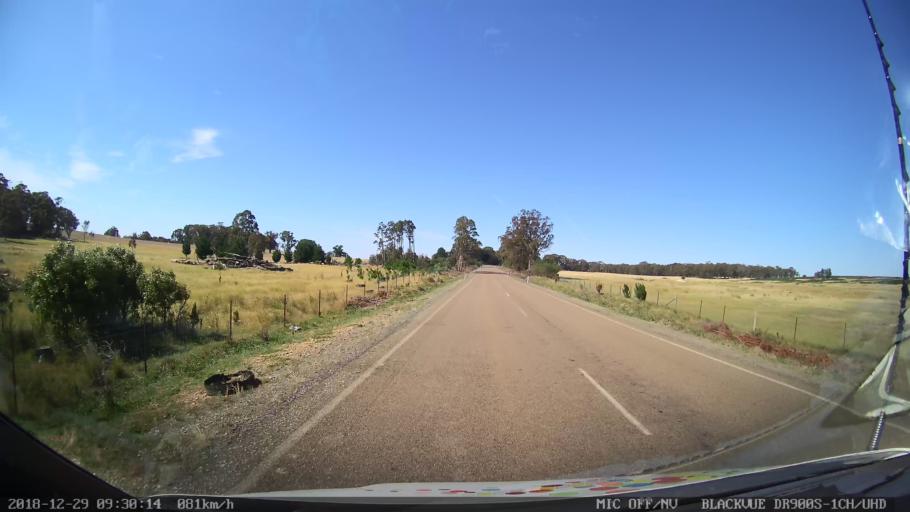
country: AU
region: New South Wales
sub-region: Upper Lachlan Shire
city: Crookwell
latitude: -34.5966
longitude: 149.3705
